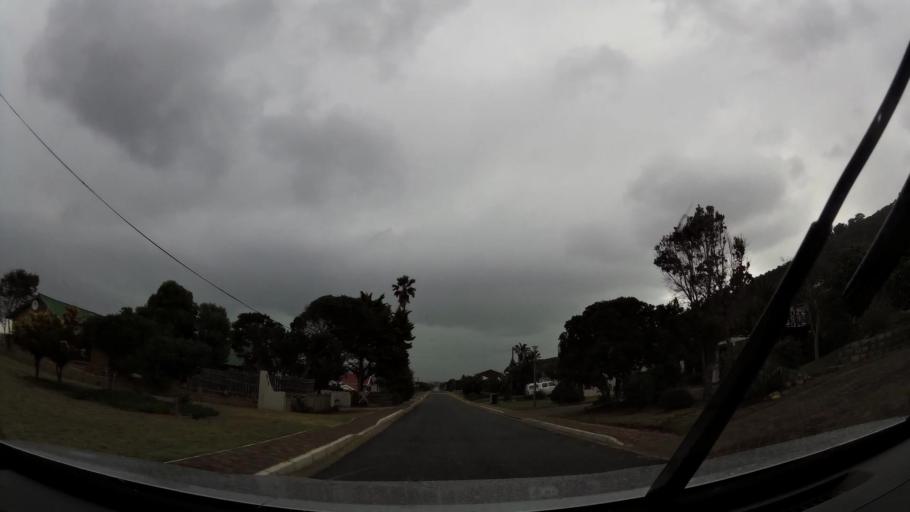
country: ZA
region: Western Cape
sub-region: Eden District Municipality
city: George
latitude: -34.0495
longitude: 22.3027
